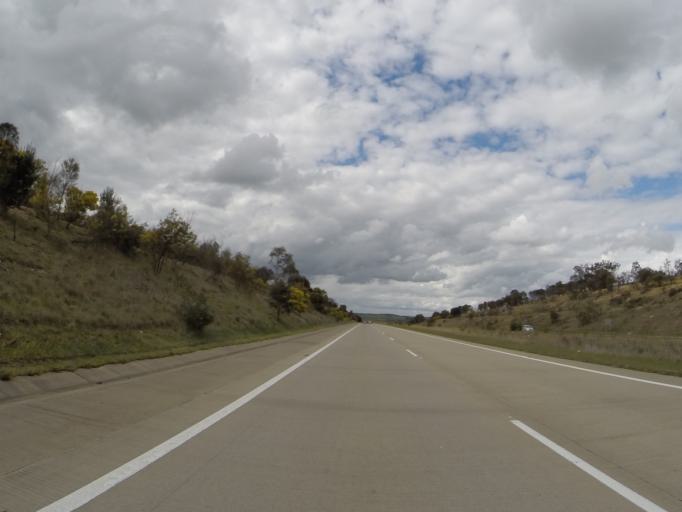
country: AU
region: New South Wales
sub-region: Yass Valley
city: Gundaroo
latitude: -34.8192
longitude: 149.4072
